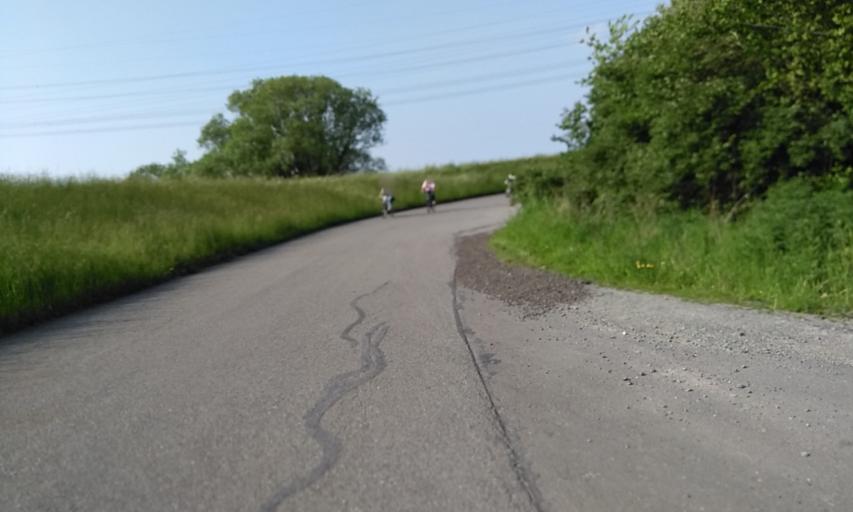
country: DE
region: Lower Saxony
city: Buxtehude
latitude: 53.4899
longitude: 9.7137
